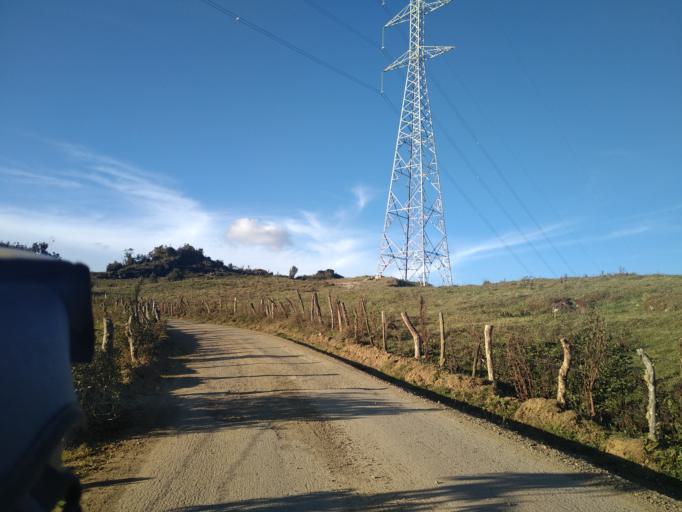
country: PE
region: Amazonas
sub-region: Provincia de Chachapoyas
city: Montevideo
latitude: -6.7146
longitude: -77.8657
